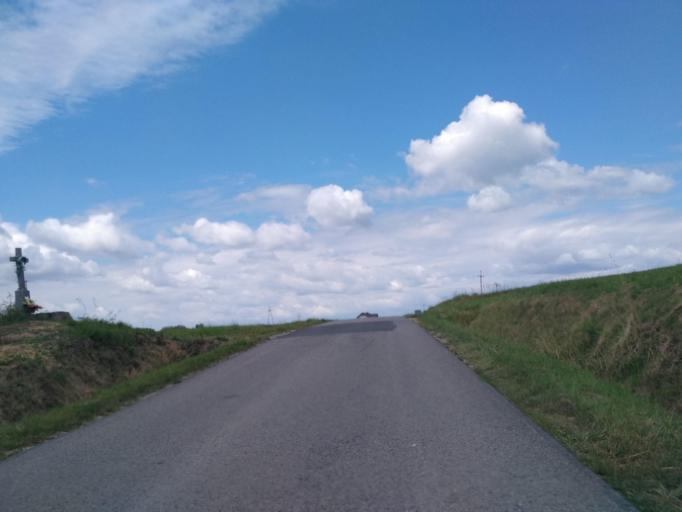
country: PL
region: Subcarpathian Voivodeship
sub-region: Powiat rzeszowski
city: Hyzne
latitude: 49.9141
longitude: 22.2158
